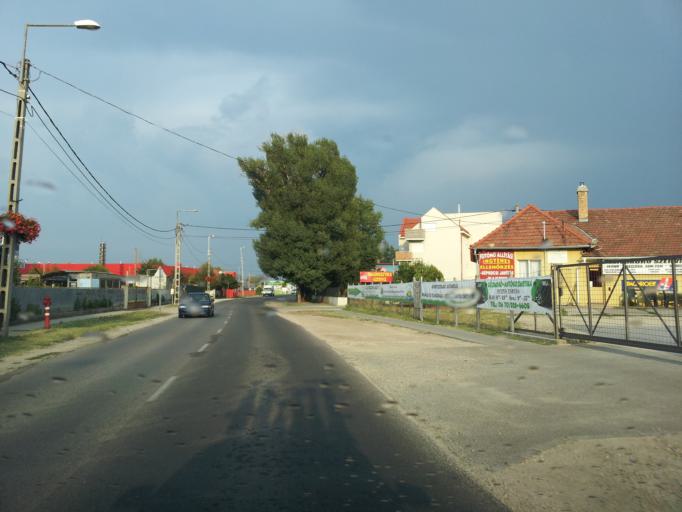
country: HU
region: Pest
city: Dunaharaszti
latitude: 47.3473
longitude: 19.1133
